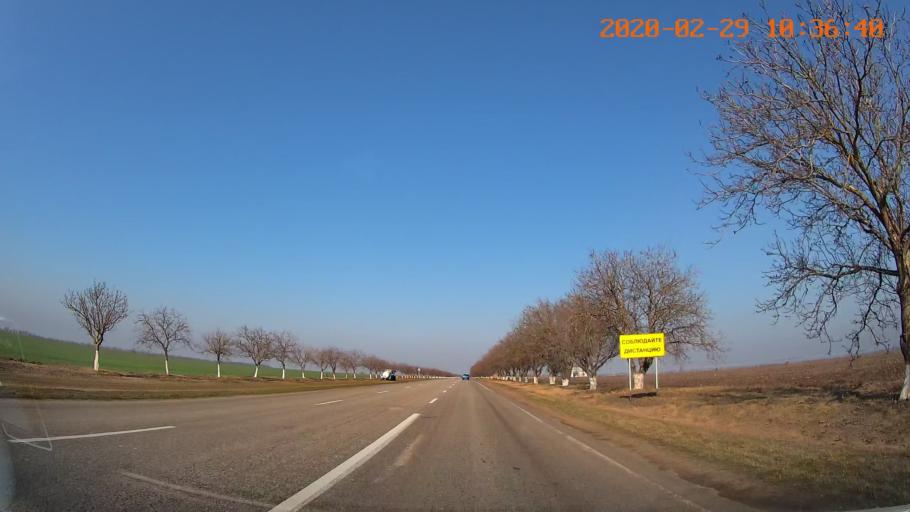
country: MD
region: Anenii Noi
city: Varnita
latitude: 46.9980
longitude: 29.5016
